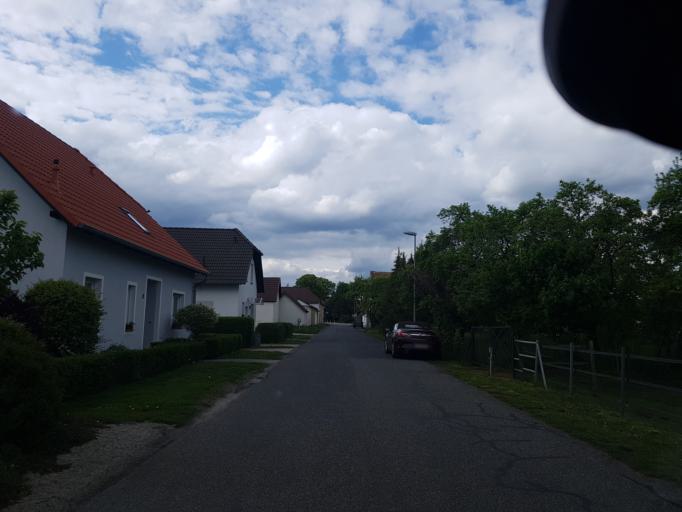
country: DE
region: Brandenburg
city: Grossraschen
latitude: 51.5863
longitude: 14.0620
